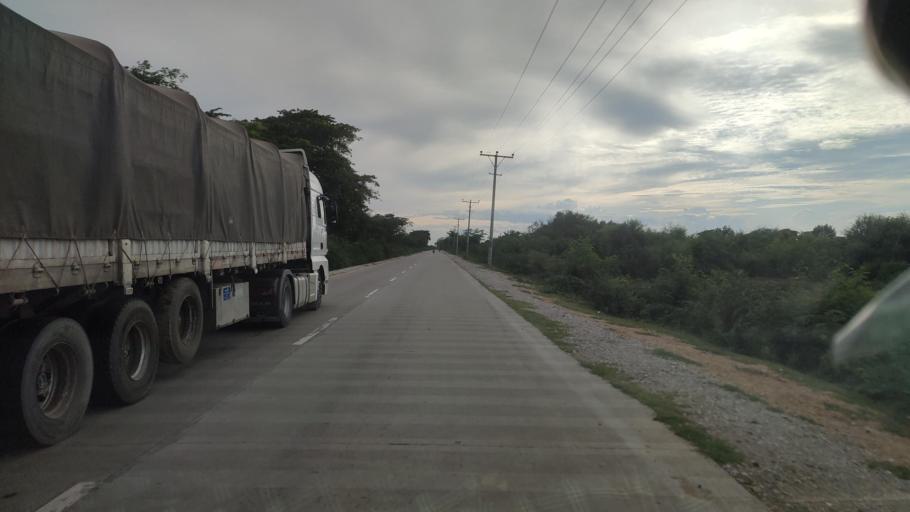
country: MM
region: Mandalay
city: Kyaukse
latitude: 21.3436
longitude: 96.0807
